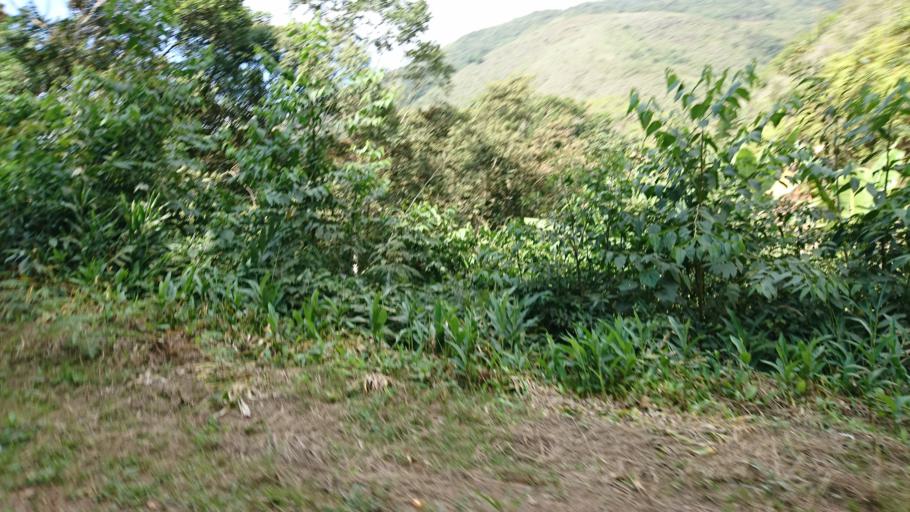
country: BO
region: La Paz
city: Coroico
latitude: -16.1244
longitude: -67.7632
